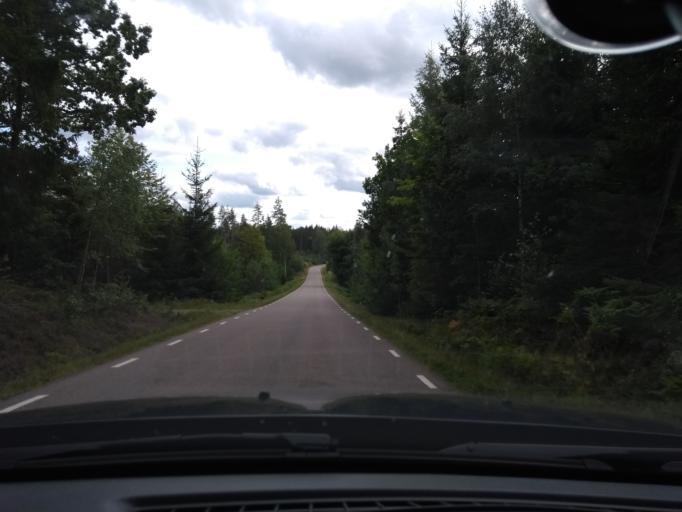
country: SE
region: Joenkoeping
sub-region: Eksjo Kommun
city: Mariannelund
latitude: 57.6190
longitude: 15.7089
